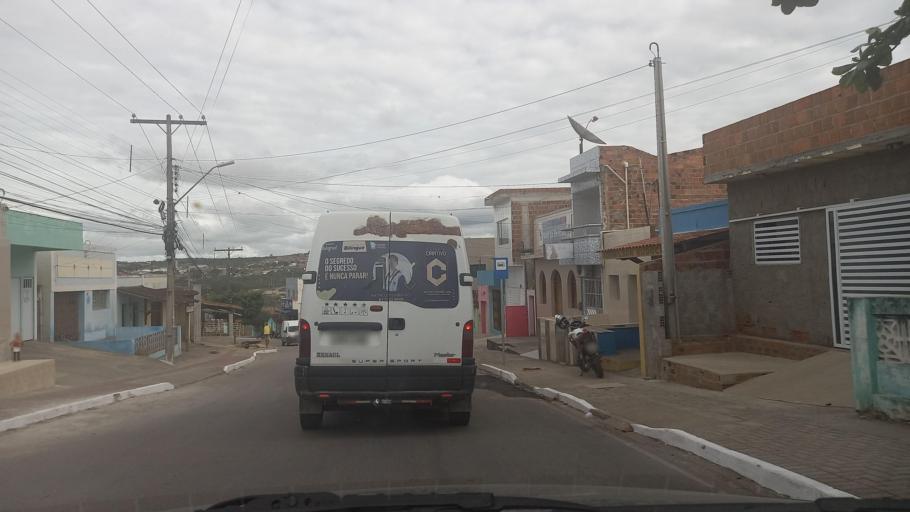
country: BR
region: Pernambuco
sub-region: Caruaru
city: Caruaru
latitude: -8.2954
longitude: -36.0300
